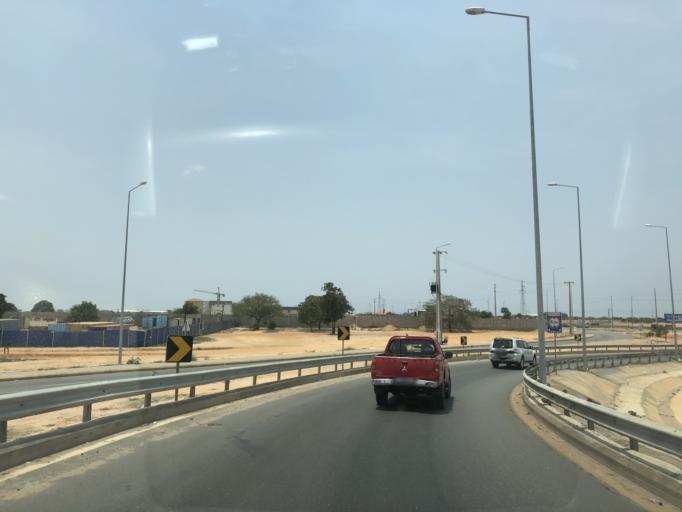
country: AO
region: Luanda
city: Luanda
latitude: -8.9749
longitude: 13.2527
